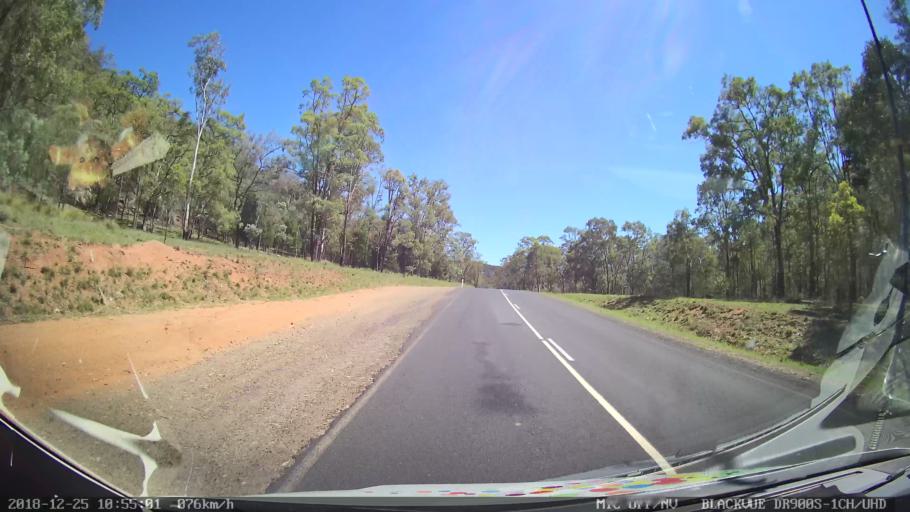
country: AU
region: New South Wales
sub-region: Upper Hunter Shire
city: Merriwa
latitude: -32.4035
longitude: 150.2730
